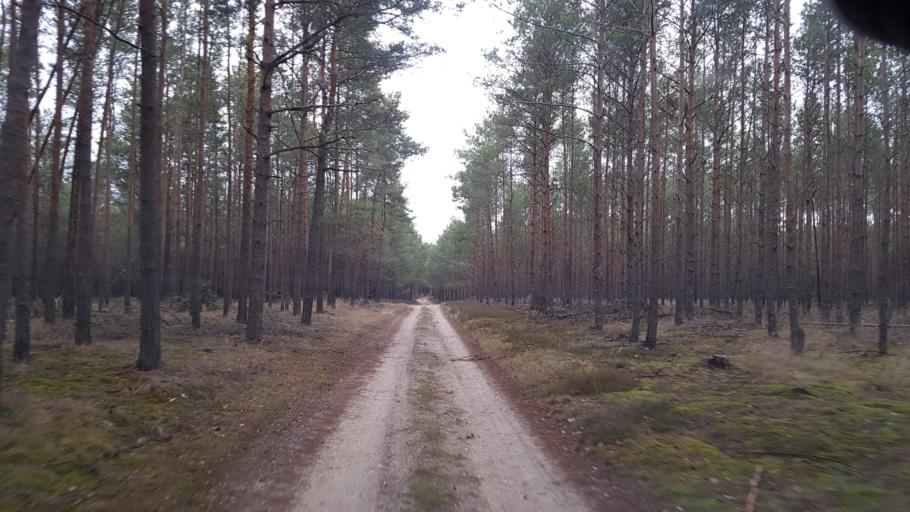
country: DE
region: Brandenburg
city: Finsterwalde
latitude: 51.6232
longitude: 13.6462
